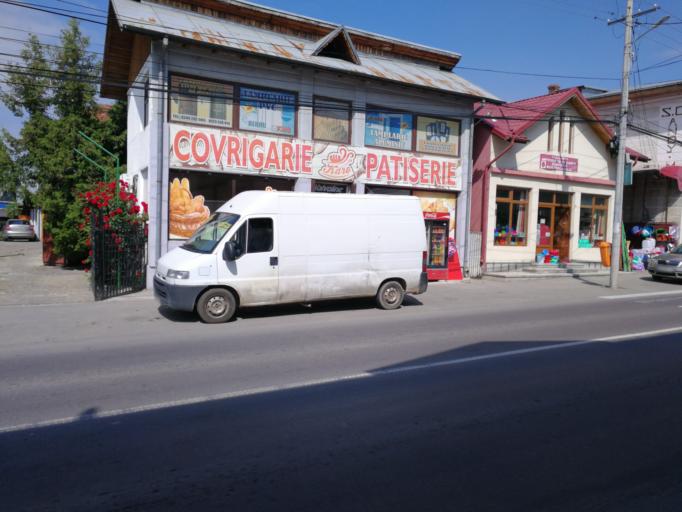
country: RO
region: Prahova
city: Valenii de Munte
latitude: 45.1900
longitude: 26.0428
